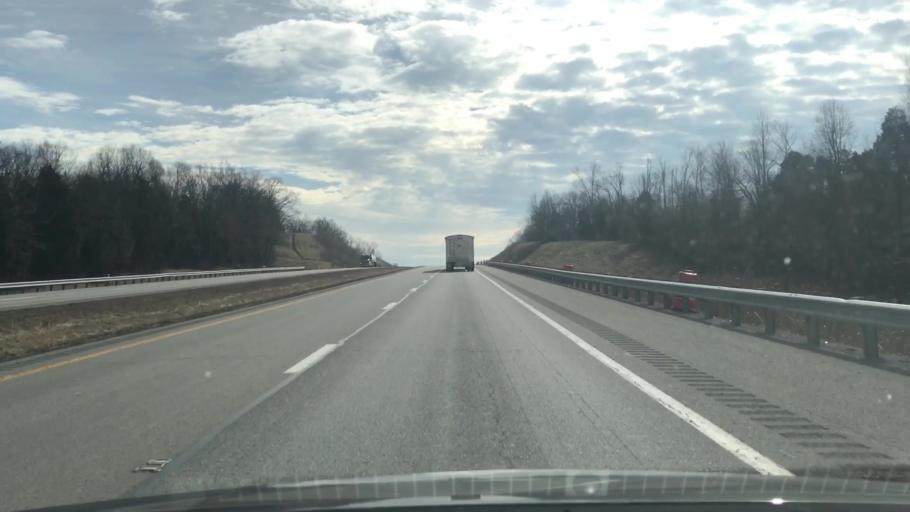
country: US
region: Kentucky
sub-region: Ohio County
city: Hartford
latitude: 37.5714
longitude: -86.9508
